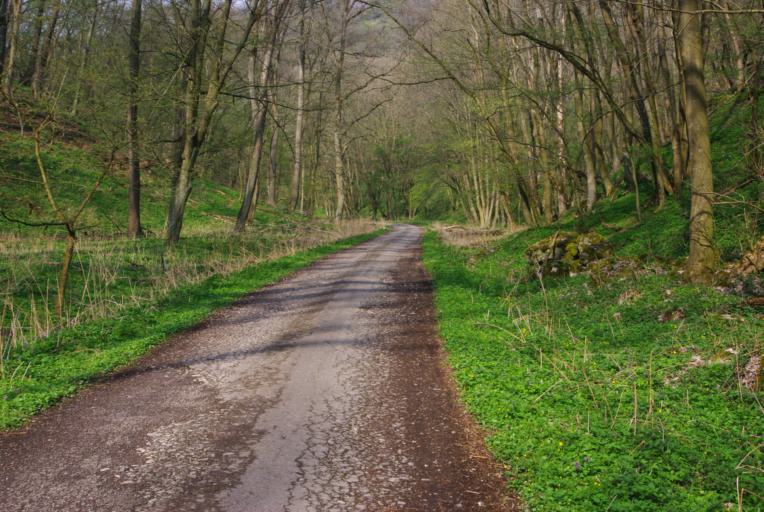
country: HU
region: Fejer
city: Szarliget
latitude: 47.4608
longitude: 18.4611
